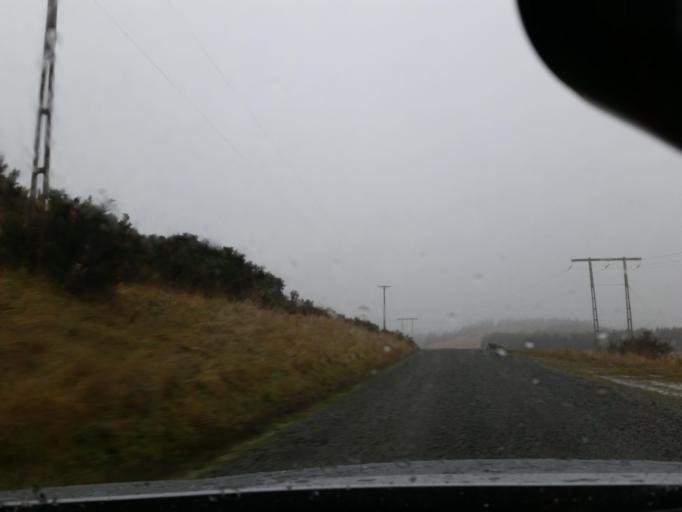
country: NZ
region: Southland
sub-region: Southland District
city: Te Anau
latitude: -45.5996
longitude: 168.0758
